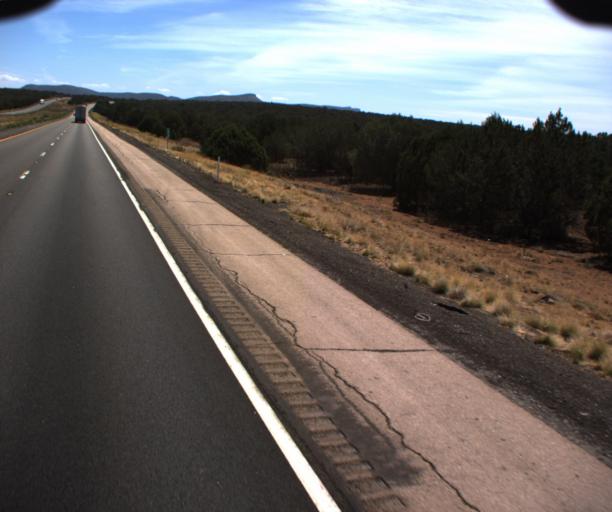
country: US
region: Arizona
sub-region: Mohave County
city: Peach Springs
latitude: 35.1909
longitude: -113.3429
